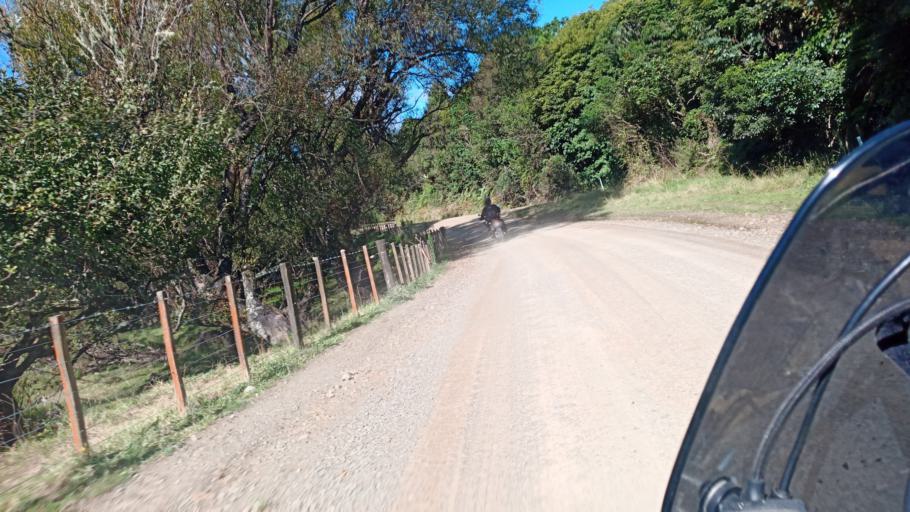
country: NZ
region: Bay of Plenty
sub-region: Opotiki District
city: Opotiki
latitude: -38.2564
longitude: 177.5545
